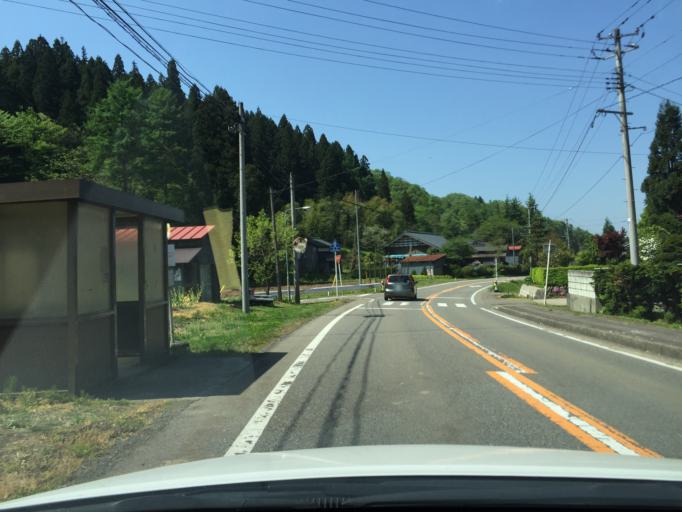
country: JP
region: Niigata
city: Kamo
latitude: 37.6358
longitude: 139.1089
